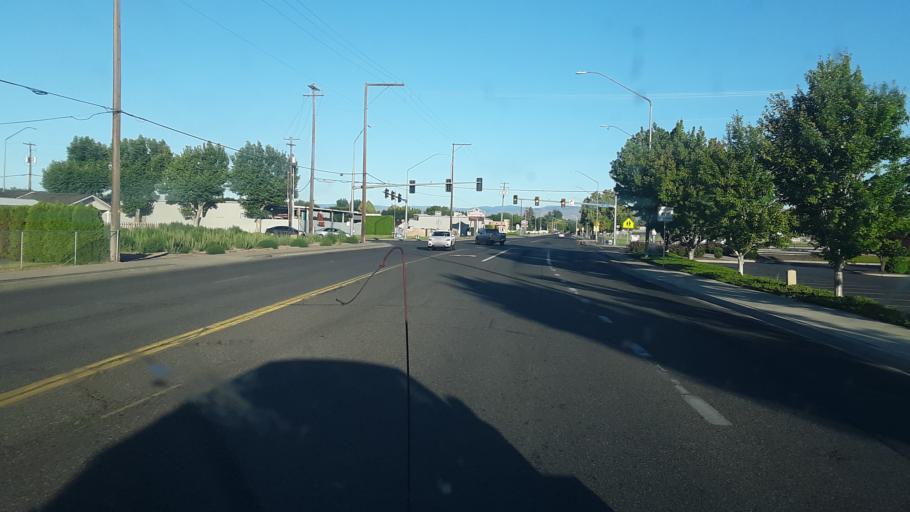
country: US
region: Washington
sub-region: Yakima County
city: West Valley
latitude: 46.5859
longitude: -120.6031
